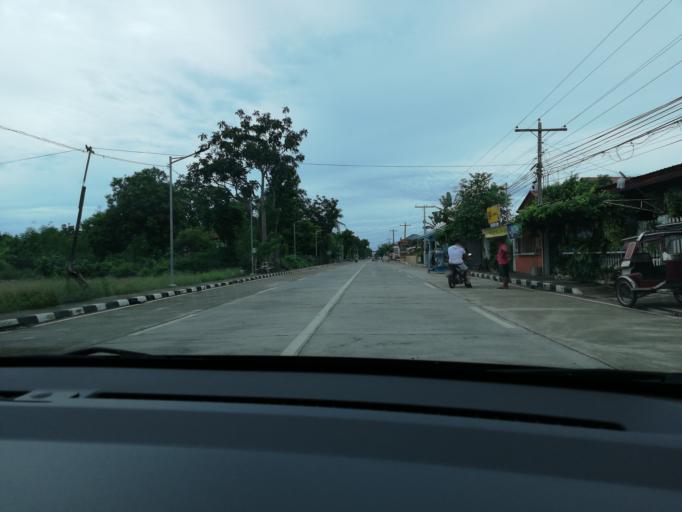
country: PH
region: Ilocos
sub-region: Province of Ilocos Sur
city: San Vicente
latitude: 17.5836
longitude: 120.3731
